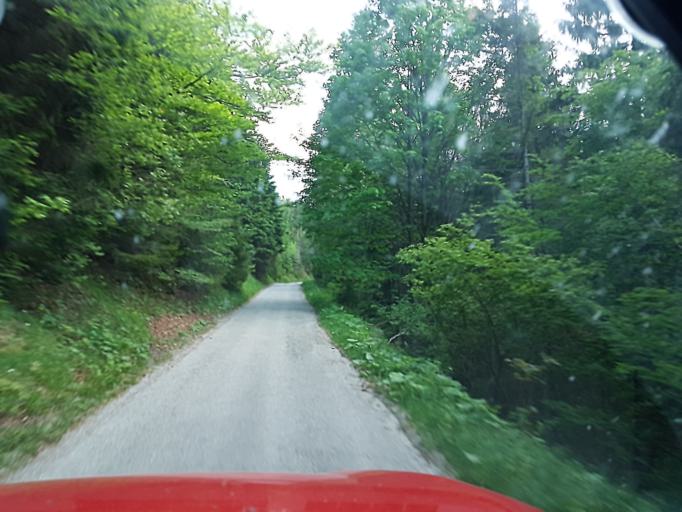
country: SK
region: Zilinsky
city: Ruzomberok
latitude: 49.0521
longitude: 19.2744
